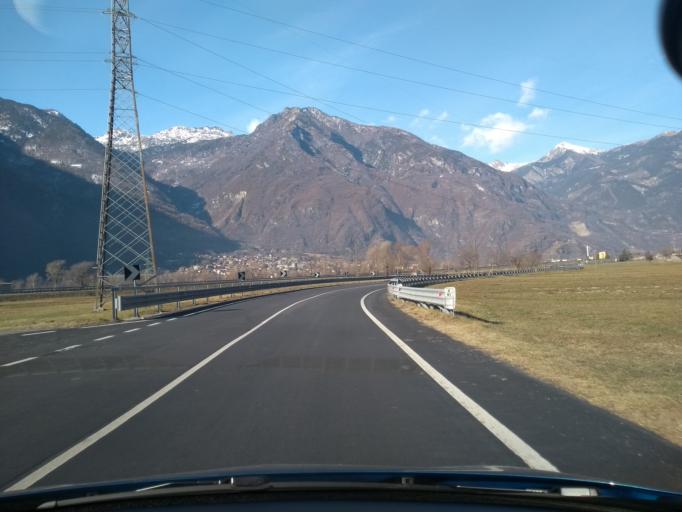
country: IT
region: Aosta Valley
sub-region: Valle d'Aosta
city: Arnad
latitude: 45.6530
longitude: 7.7040
